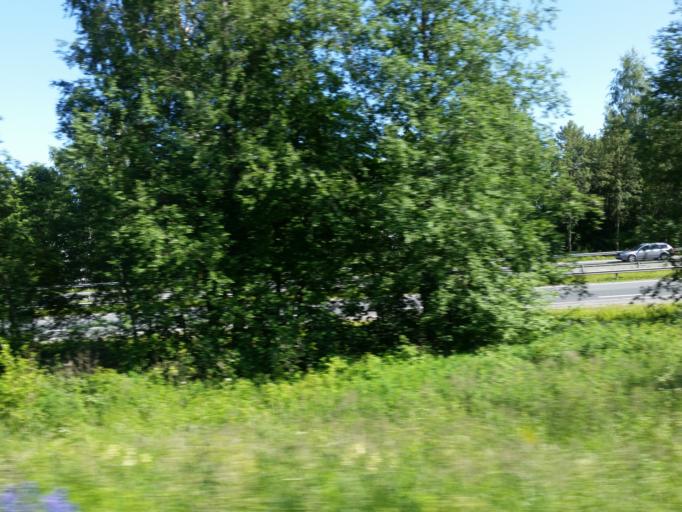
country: FI
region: Northern Savo
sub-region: Kuopio
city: Kuopio
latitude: 62.8981
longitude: 27.6538
